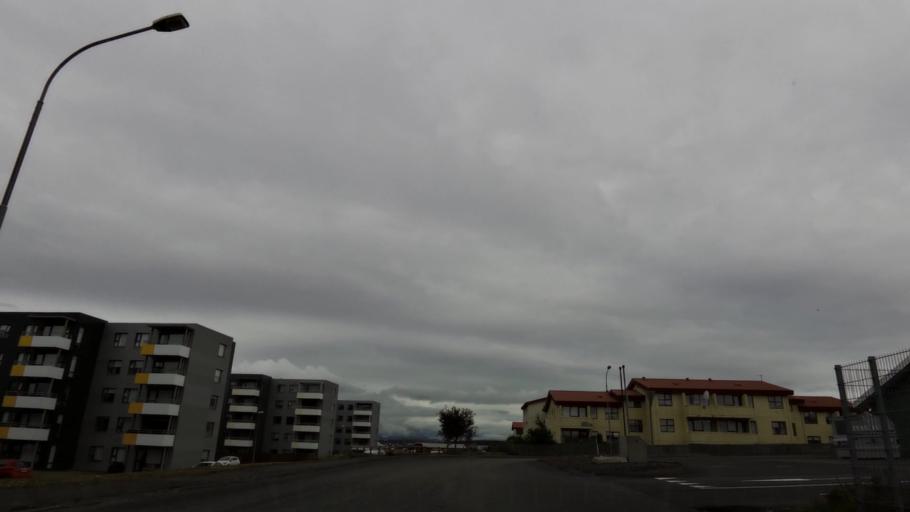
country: IS
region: Capital Region
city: Hafnarfjoerdur
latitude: 64.0592
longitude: -21.9720
